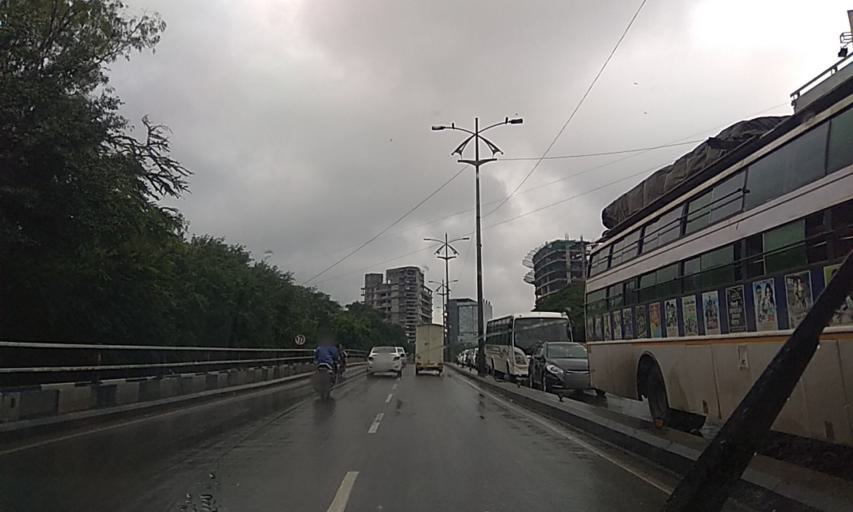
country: IN
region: Maharashtra
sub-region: Pune Division
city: Shivaji Nagar
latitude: 18.5312
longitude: 73.8455
